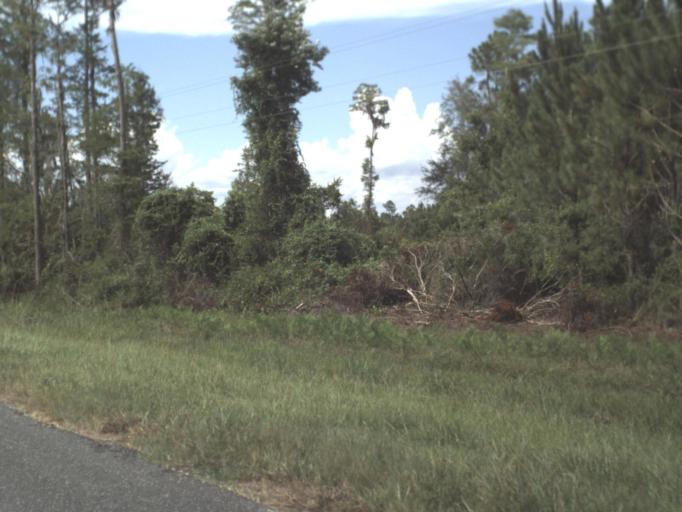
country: US
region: Florida
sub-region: Taylor County
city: Perry
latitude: 30.2312
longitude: -83.6173
